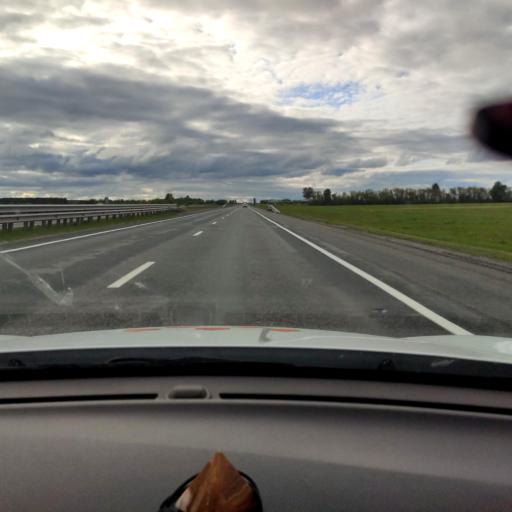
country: RU
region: Tatarstan
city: Pestretsy
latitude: 55.5302
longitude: 49.7783
